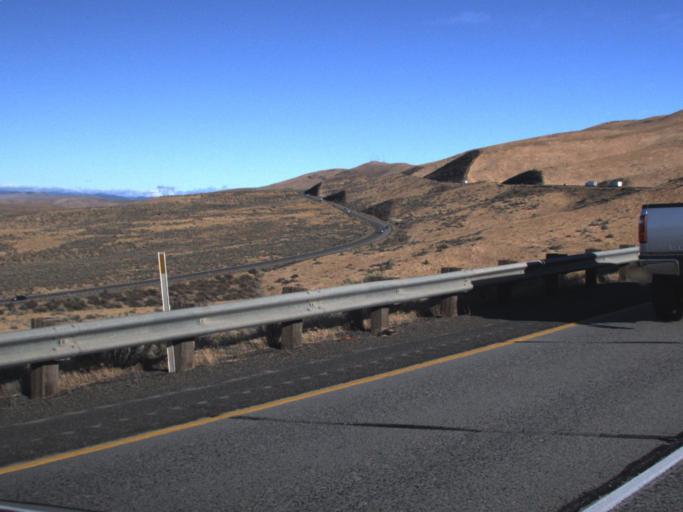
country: US
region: Washington
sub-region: Kittitas County
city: Kittitas
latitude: 46.8576
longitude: -120.3932
